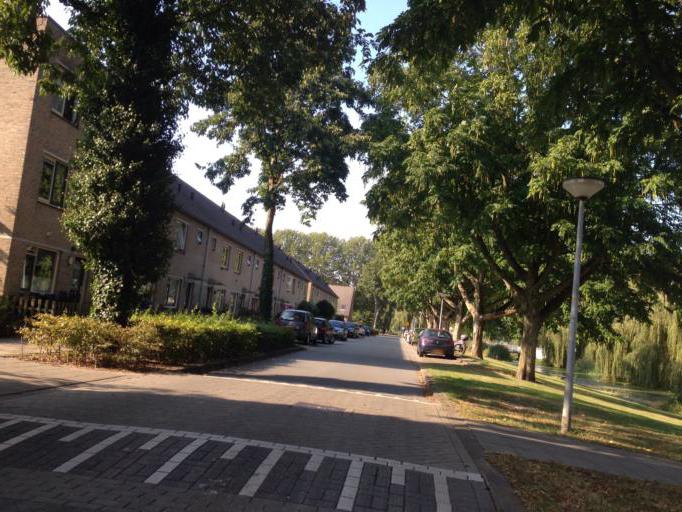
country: NL
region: Flevoland
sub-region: Gemeente Almere
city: Almere Stad
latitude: 52.3943
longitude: 5.2579
